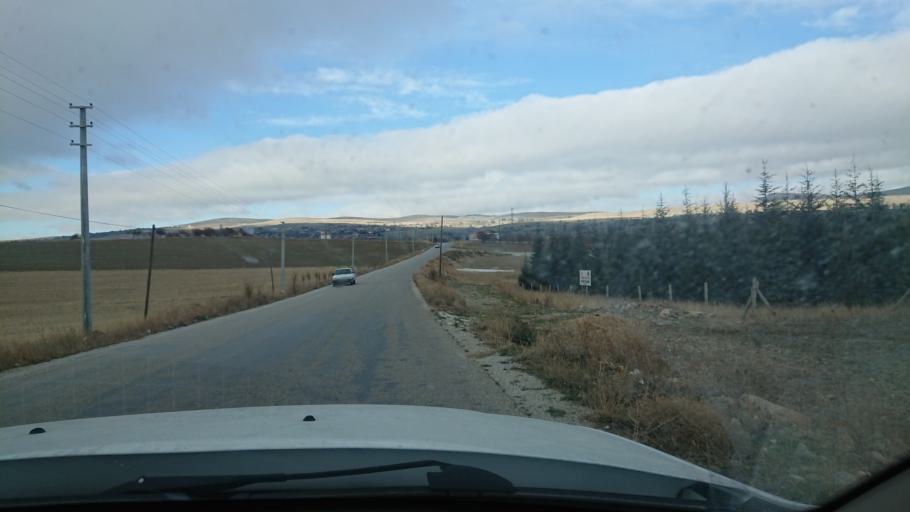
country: TR
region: Aksaray
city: Ortakoy
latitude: 38.7484
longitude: 34.0274
